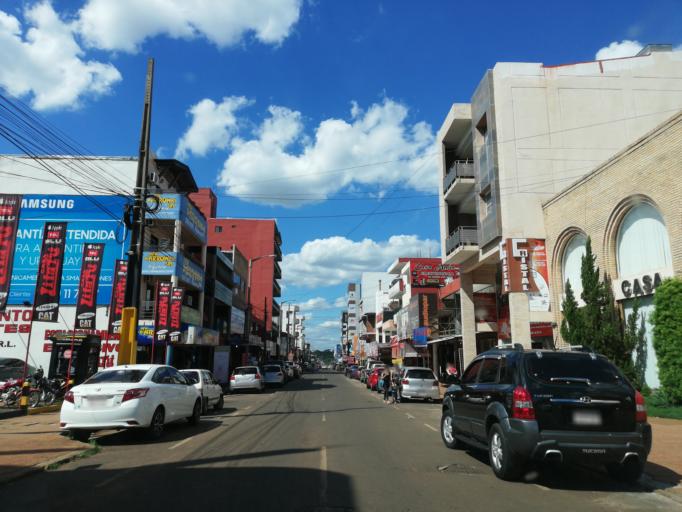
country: PY
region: Itapua
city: Encarnacion
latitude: -27.3613
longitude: -55.8505
